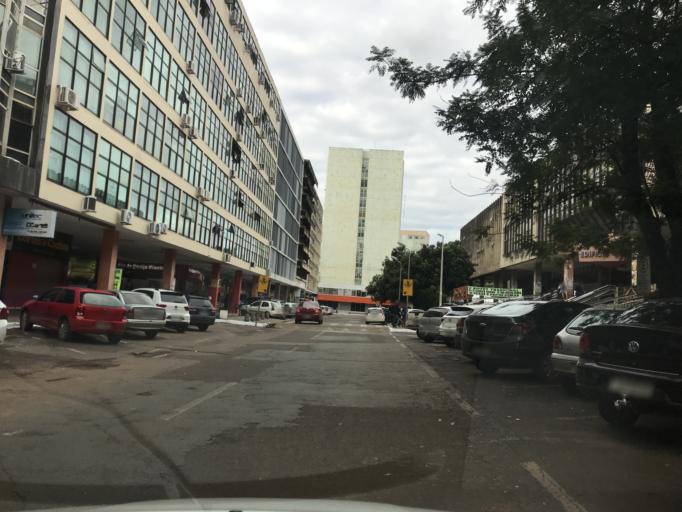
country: BR
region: Federal District
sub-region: Brasilia
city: Brasilia
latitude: -15.7977
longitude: -47.8875
